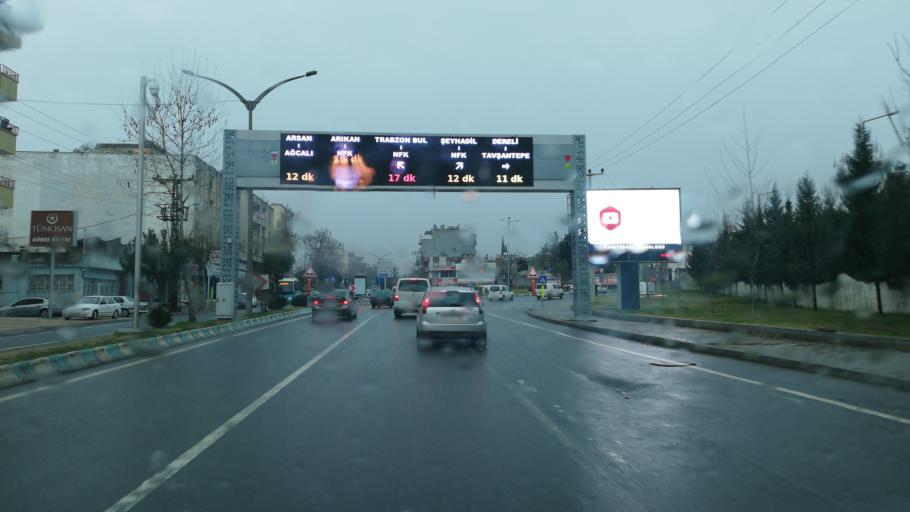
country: TR
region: Kahramanmaras
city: Kahramanmaras
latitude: 37.5658
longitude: 36.9502
